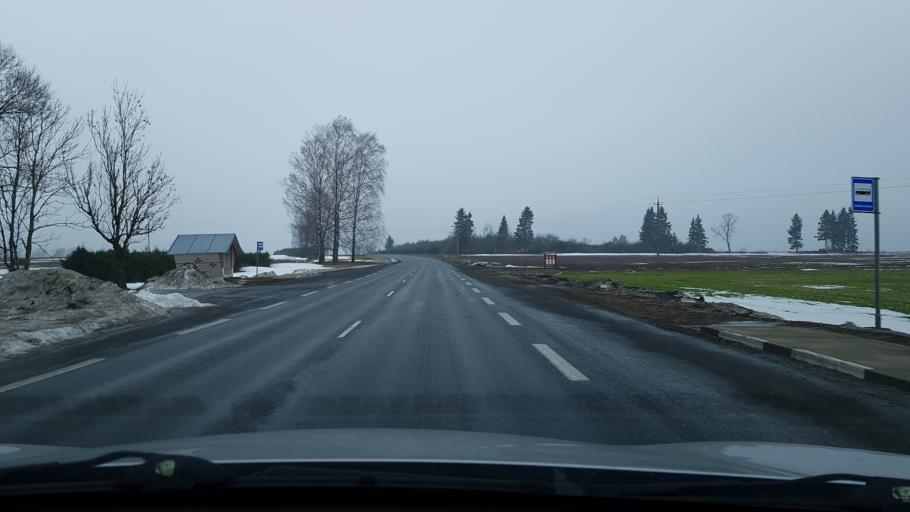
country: EE
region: Viljandimaa
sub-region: Viiratsi vald
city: Viiratsi
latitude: 58.2506
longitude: 25.8366
